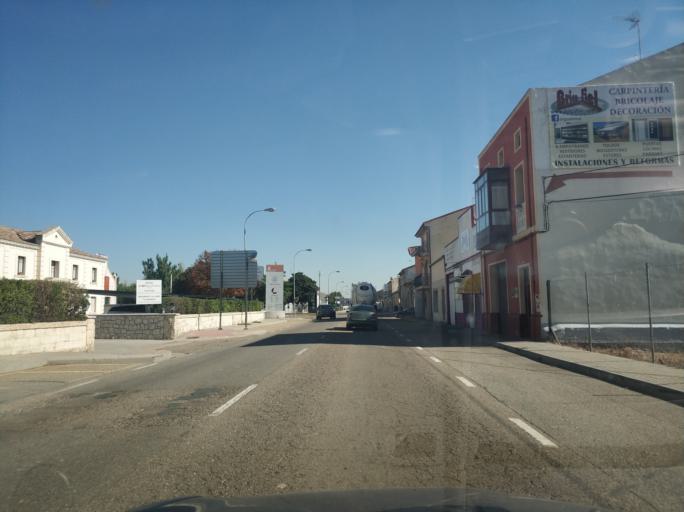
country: ES
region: Castille and Leon
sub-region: Provincia de Valladolid
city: Penafiel
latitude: 41.6016
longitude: -4.1160
